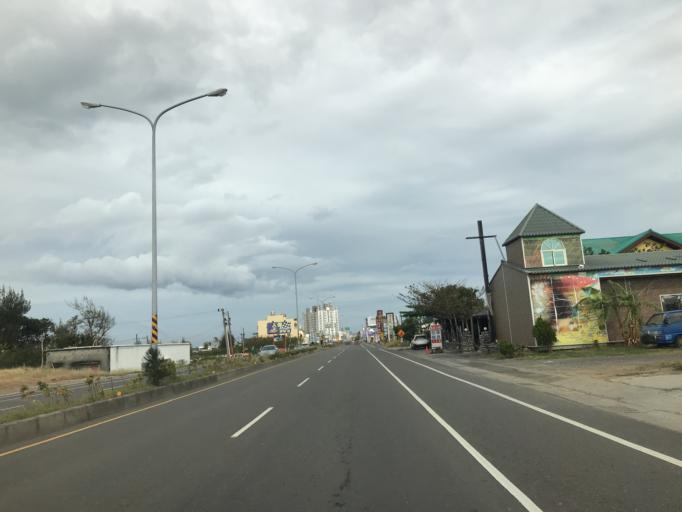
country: TW
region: Taiwan
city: Hengchun
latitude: 21.9859
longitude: 120.7496
